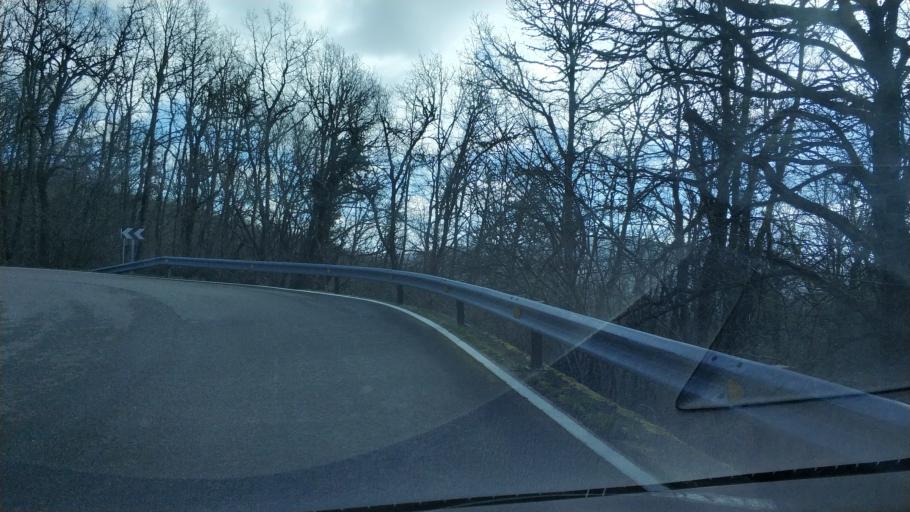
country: ES
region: Cantabria
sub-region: Provincia de Cantabria
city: Mataporquera
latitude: 42.9033
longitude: -4.0517
